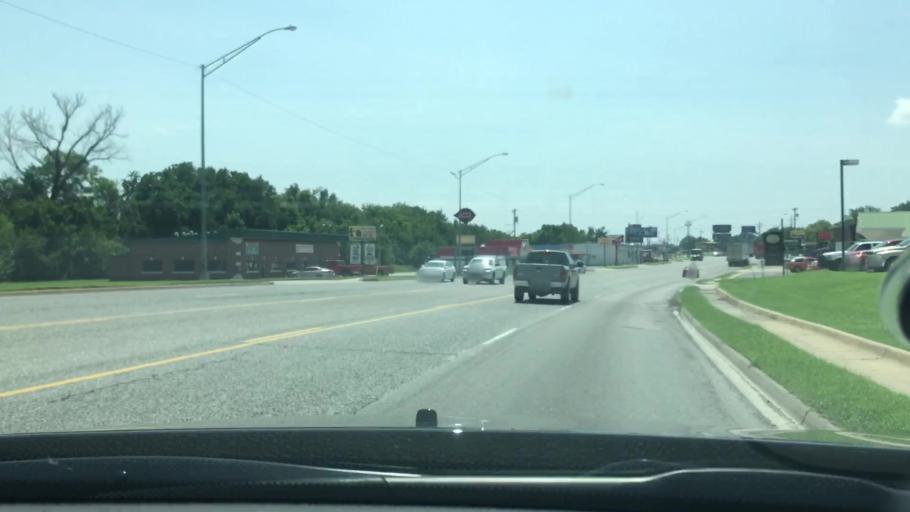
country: US
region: Oklahoma
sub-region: Atoka County
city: Atoka
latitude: 34.3798
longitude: -96.1311
